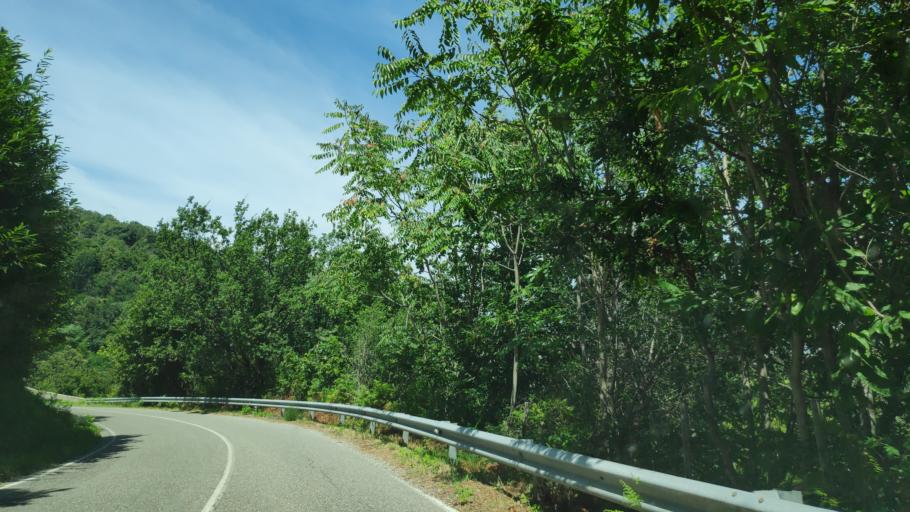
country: IT
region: Calabria
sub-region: Provincia di Catanzaro
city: Palermiti
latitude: 38.7439
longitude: 16.4514
